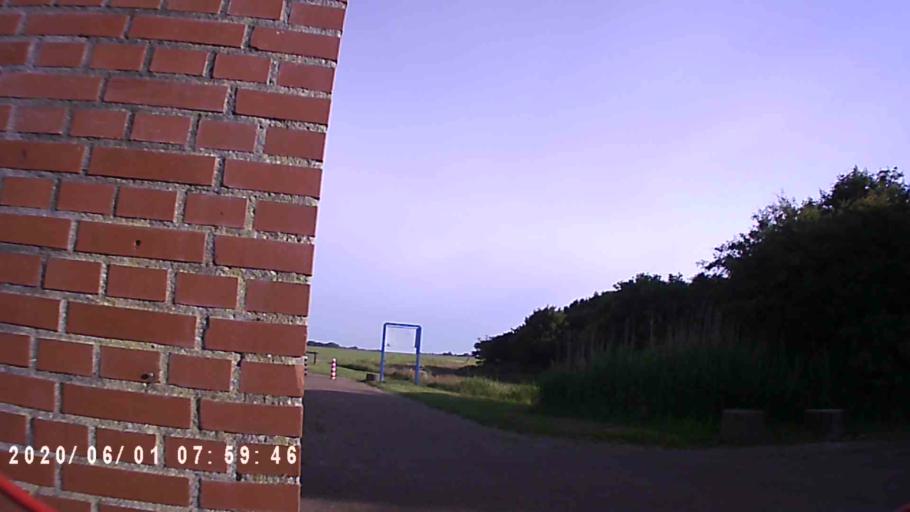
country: NL
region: Friesland
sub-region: Gemeente Dantumadiel
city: Rinsumageast
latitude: 53.2828
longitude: 5.9370
